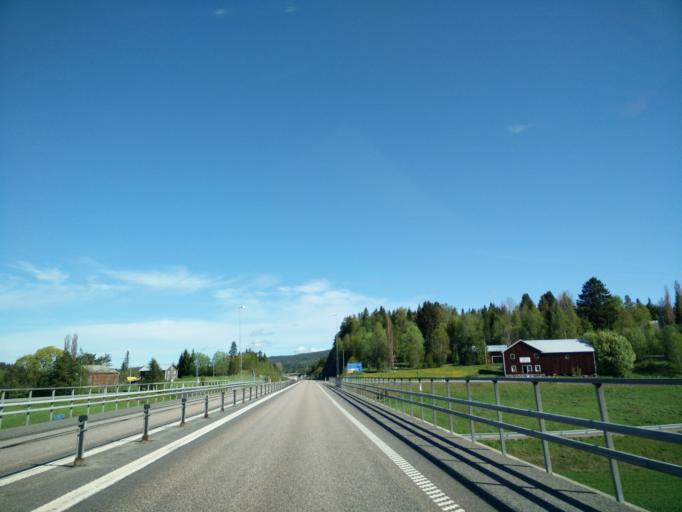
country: SE
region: Vaesternorrland
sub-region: Kramfors Kommun
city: Nordingra
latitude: 62.9259
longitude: 18.0986
